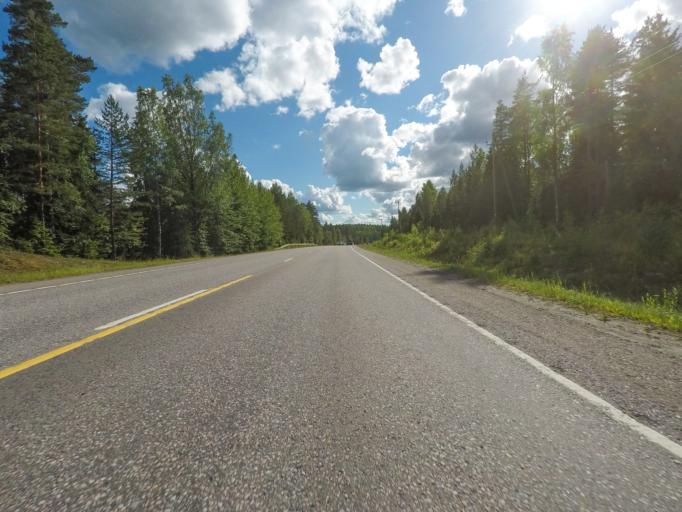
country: FI
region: Uusimaa
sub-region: Helsinki
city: Nurmijaervi
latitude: 60.5245
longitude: 24.6669
